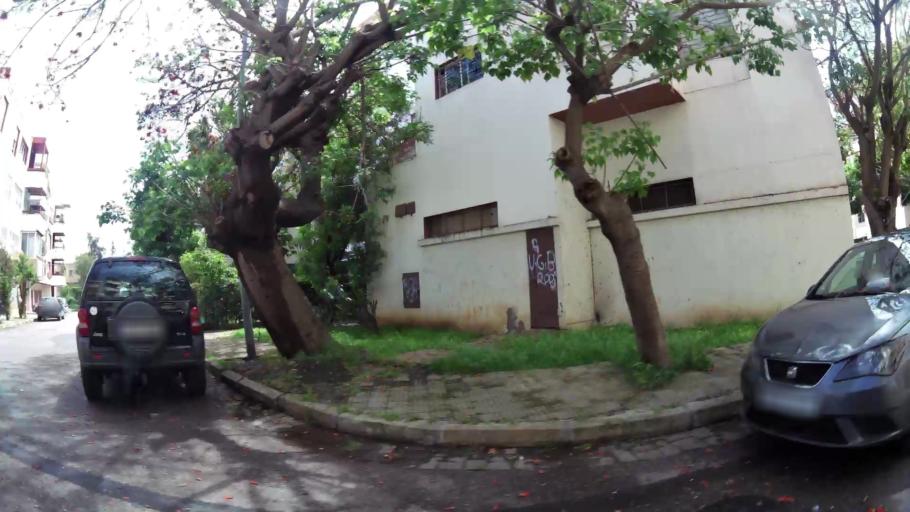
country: MA
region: Grand Casablanca
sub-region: Casablanca
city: Casablanca
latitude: 33.5681
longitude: -7.6319
